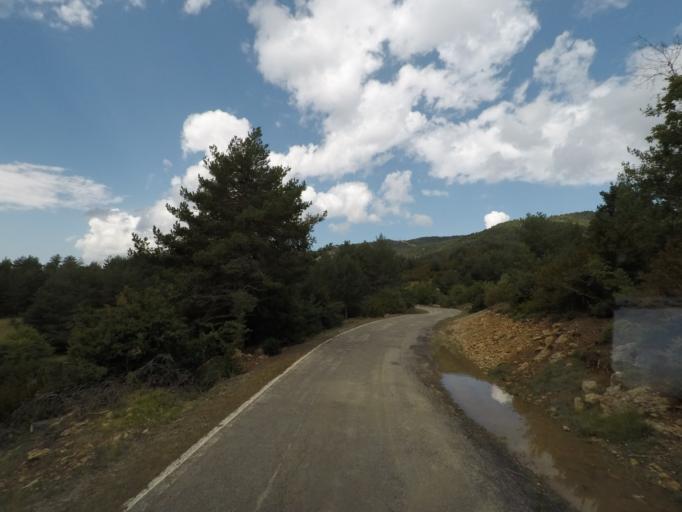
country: ES
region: Aragon
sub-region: Provincia de Huesca
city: Fiscal
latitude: 42.4004
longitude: -0.0512
